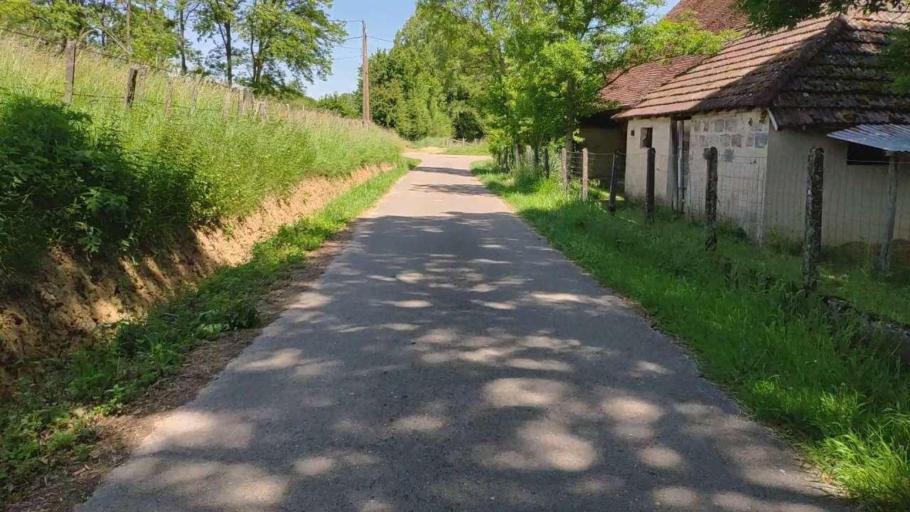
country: FR
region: Franche-Comte
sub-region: Departement du Jura
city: Bletterans
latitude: 46.8003
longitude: 5.3884
